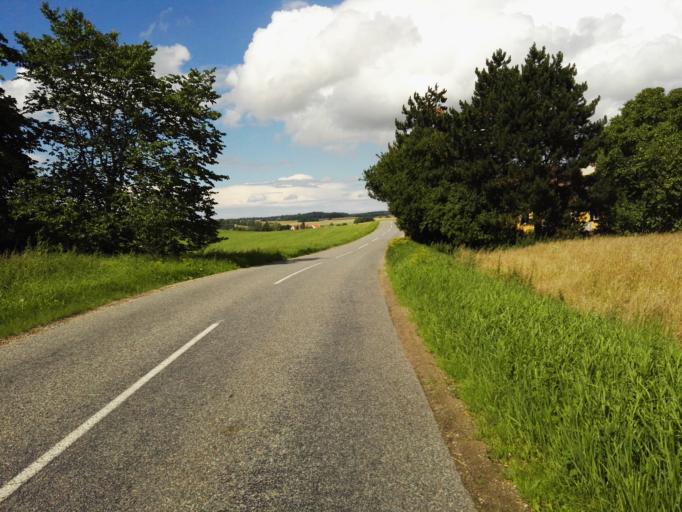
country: DK
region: Capital Region
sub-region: Egedal Kommune
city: Vekso
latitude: 55.7845
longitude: 12.2339
